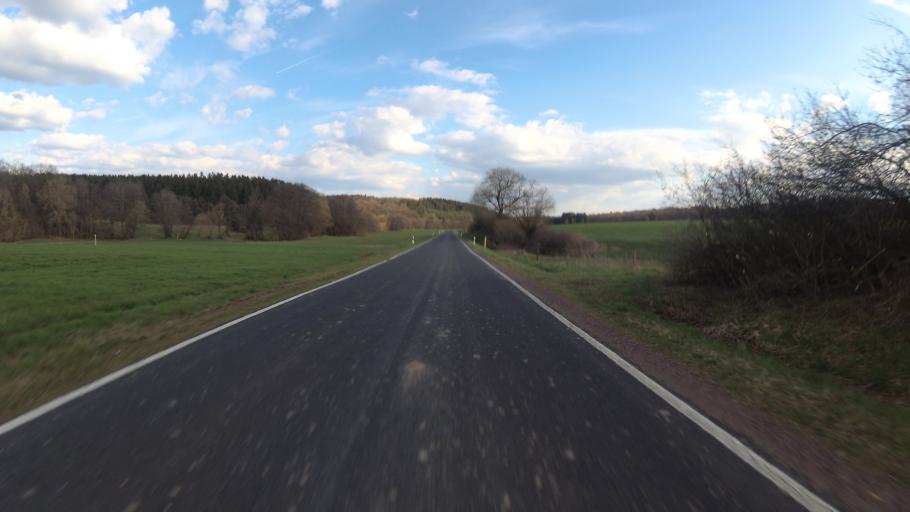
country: DE
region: Rheinland-Pfalz
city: Darscheid
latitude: 50.2076
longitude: 6.8938
